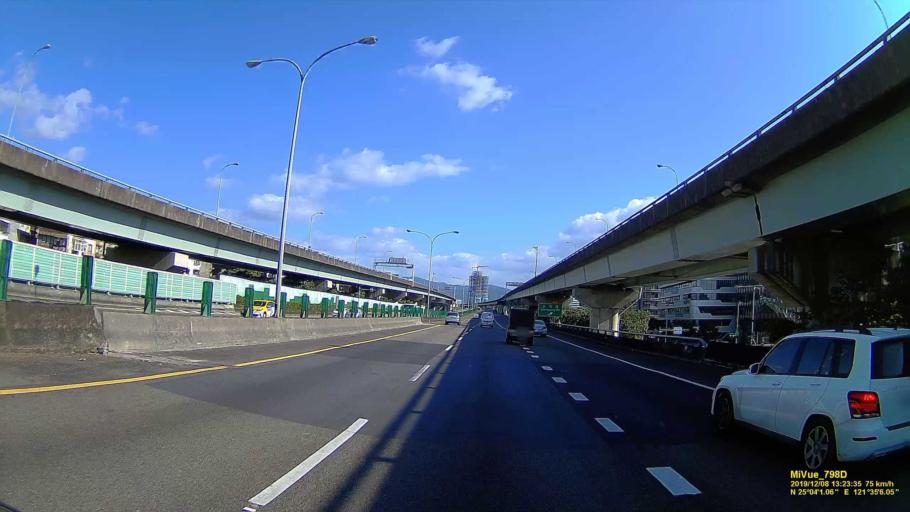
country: TW
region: Taipei
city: Taipei
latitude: 25.0668
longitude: 121.5855
